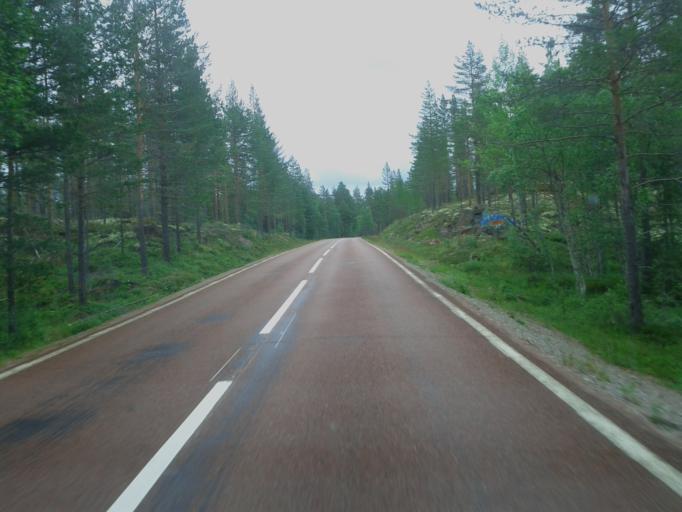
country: NO
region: Hedmark
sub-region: Trysil
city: Innbygda
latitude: 61.8523
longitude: 12.6834
